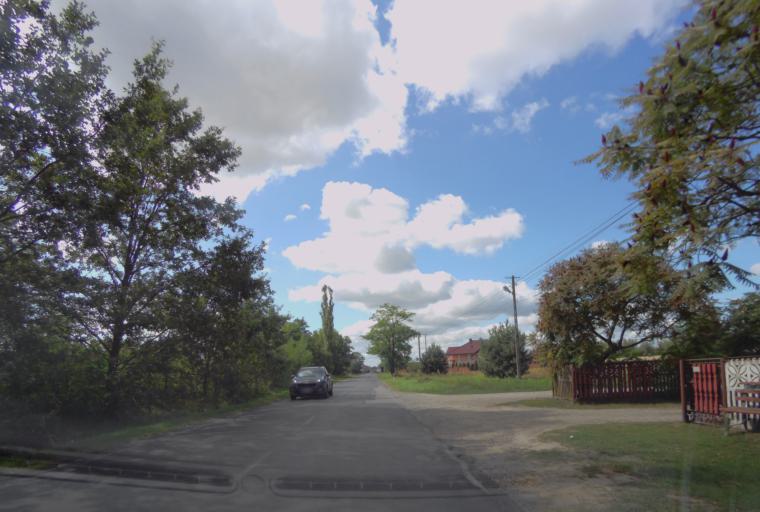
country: PL
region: Subcarpathian Voivodeship
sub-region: Powiat nizanski
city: Jezowe
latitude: 50.3709
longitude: 22.1860
